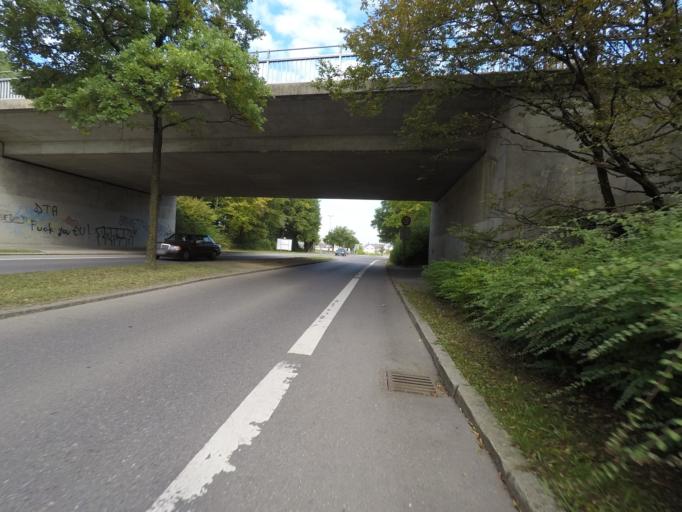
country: DE
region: Baden-Wuerttemberg
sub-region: Tuebingen Region
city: Reutlingen
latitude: 48.5111
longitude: 9.2191
